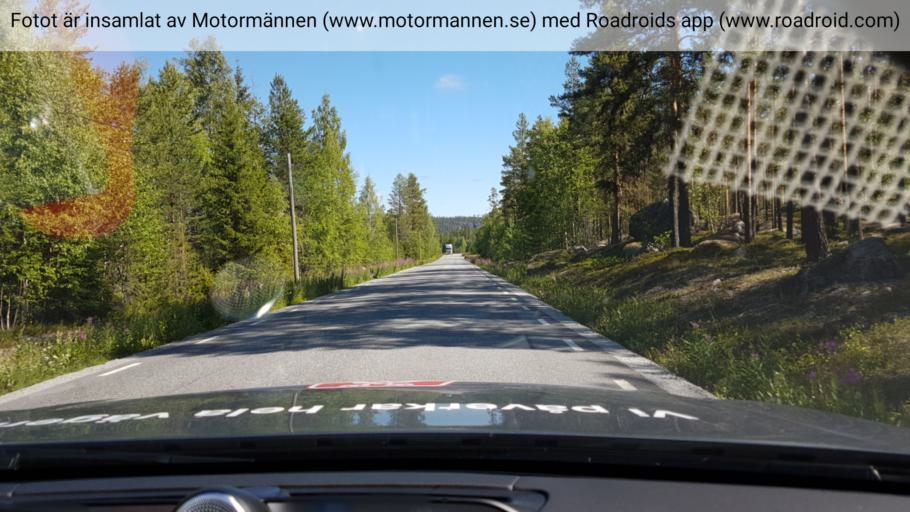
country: SE
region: Jaemtland
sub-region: Braecke Kommun
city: Braecke
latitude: 63.1539
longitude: 15.5547
